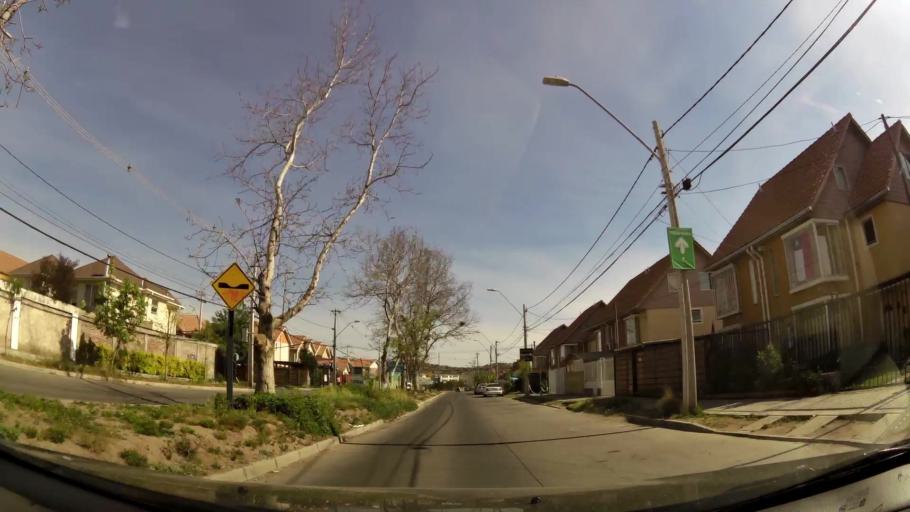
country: CL
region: Santiago Metropolitan
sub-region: Provincia de Cordillera
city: Puente Alto
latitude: -33.5931
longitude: -70.5441
